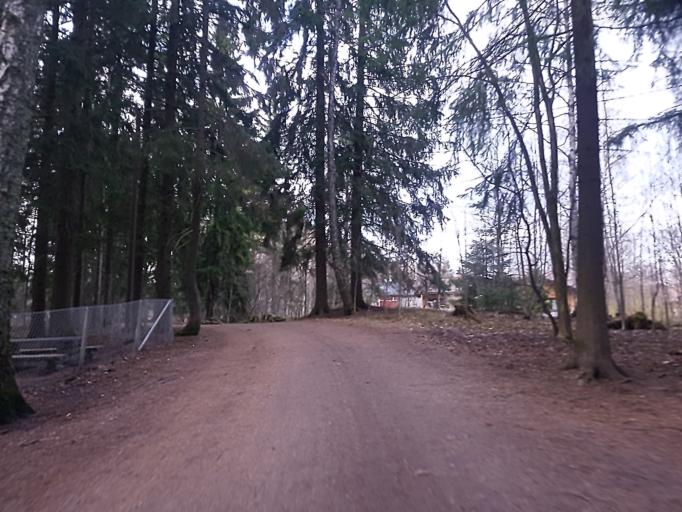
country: FI
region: Uusimaa
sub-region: Helsinki
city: Helsinki
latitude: 60.2400
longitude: 24.9137
